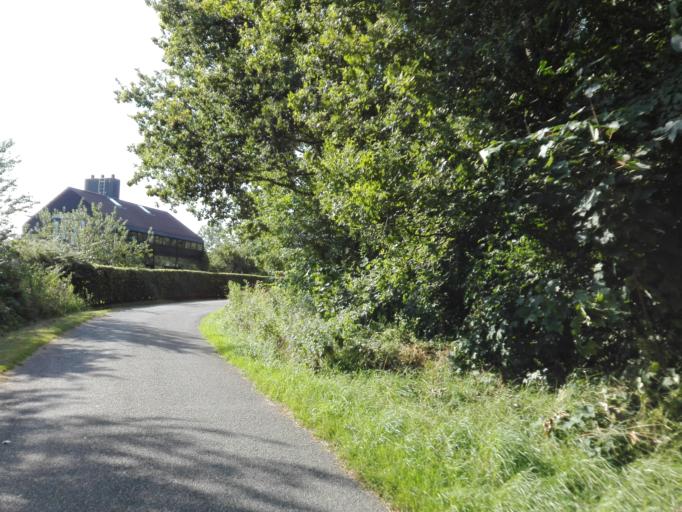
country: DK
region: Central Jutland
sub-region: Arhus Kommune
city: Lystrup
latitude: 56.2076
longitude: 10.2059
